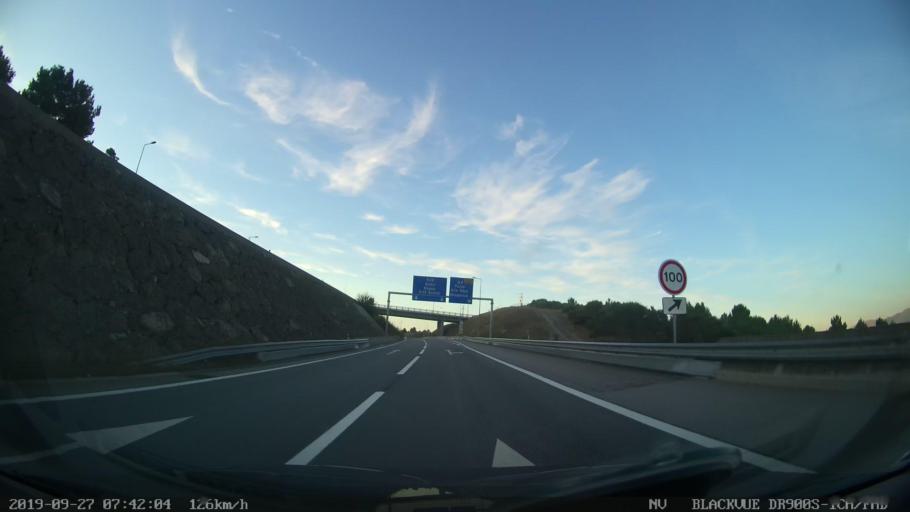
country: PT
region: Vila Real
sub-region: Vila Real
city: Vila Real
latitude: 41.2974
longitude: -7.6941
